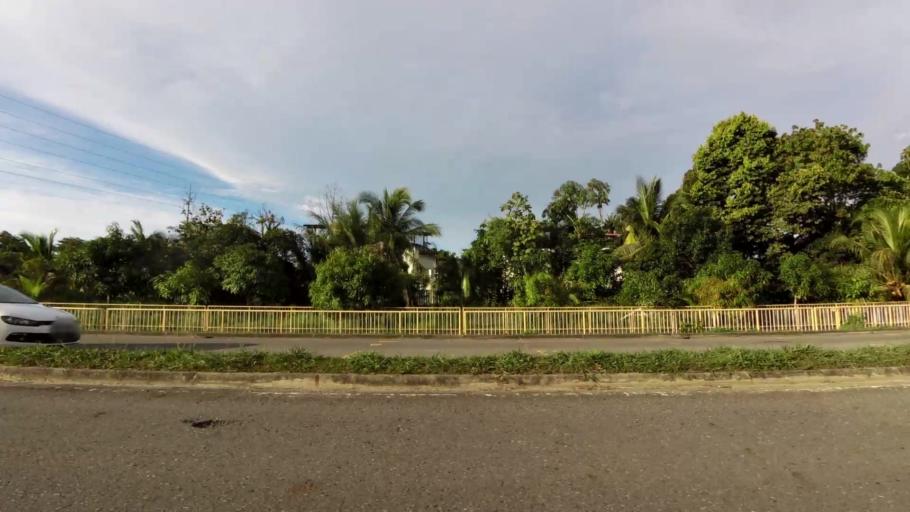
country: BN
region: Brunei and Muara
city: Bandar Seri Begawan
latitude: 4.9763
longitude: 114.9836
